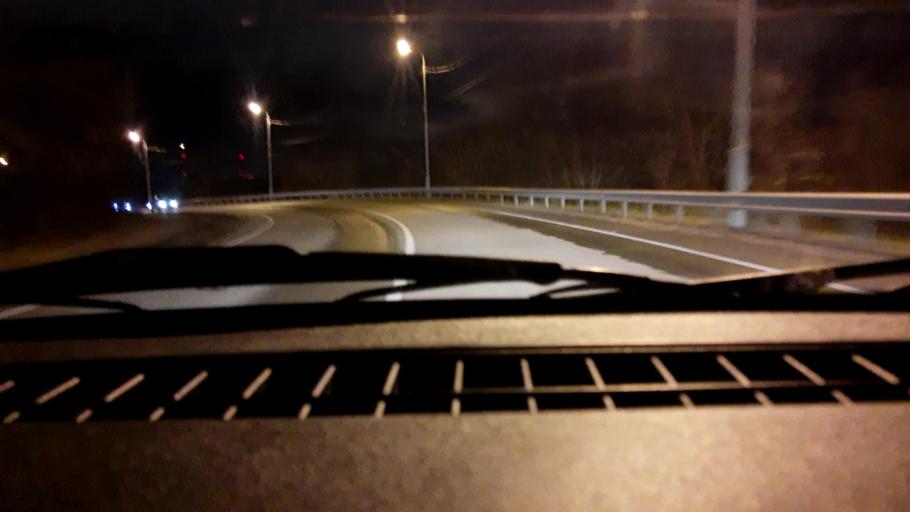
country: RU
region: Bashkortostan
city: Ufa
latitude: 54.8837
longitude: 56.0523
